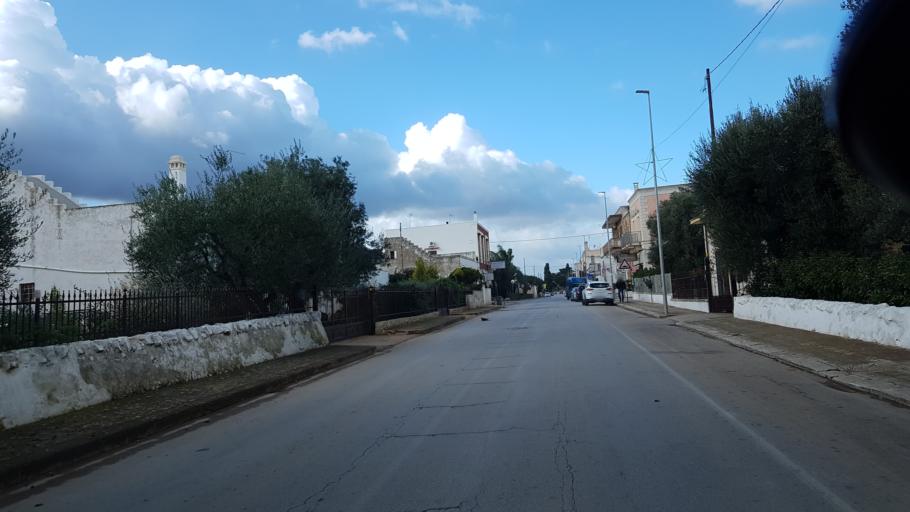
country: IT
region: Apulia
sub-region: Provincia di Brindisi
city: Montalbano
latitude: 40.7908
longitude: 17.4618
